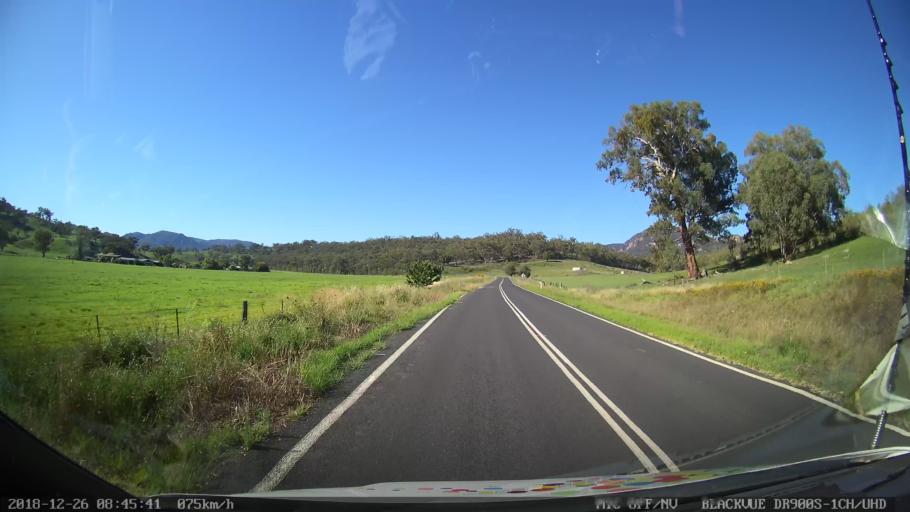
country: AU
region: New South Wales
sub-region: Mid-Western Regional
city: Kandos
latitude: -32.5280
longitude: 150.0866
